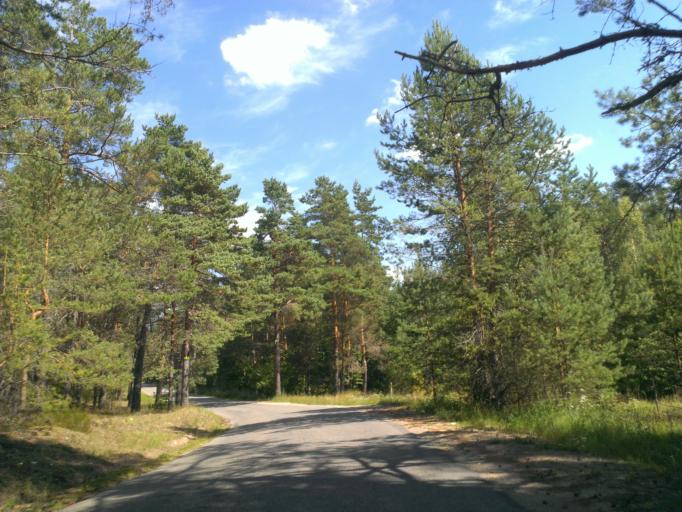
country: LV
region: Adazi
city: Adazi
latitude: 57.0971
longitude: 24.3711
